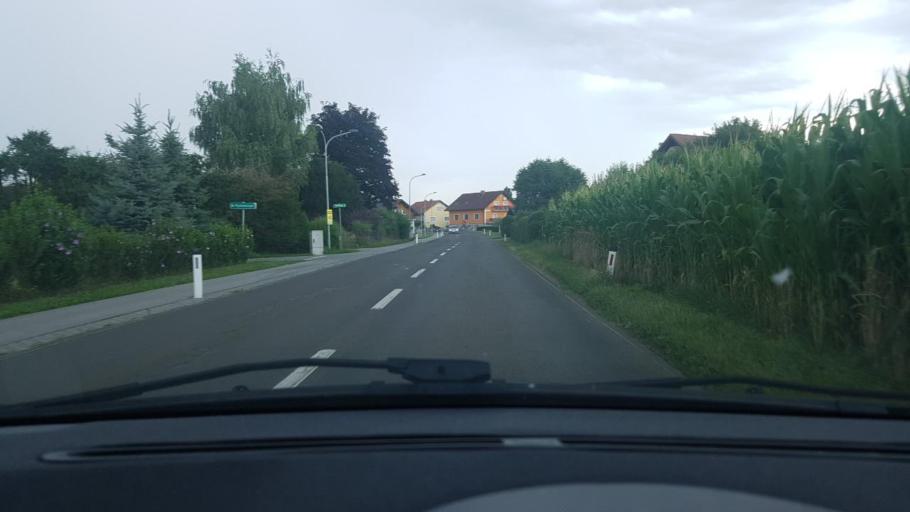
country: AT
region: Styria
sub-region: Politischer Bezirk Graz-Umgebung
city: Wundschuh
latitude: 46.9348
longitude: 15.4470
